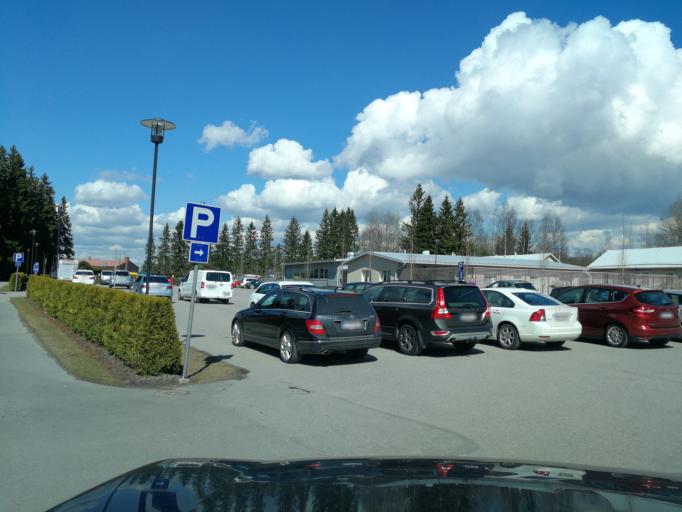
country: FI
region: Uusimaa
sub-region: Helsinki
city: Vantaa
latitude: 60.2399
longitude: 25.0266
